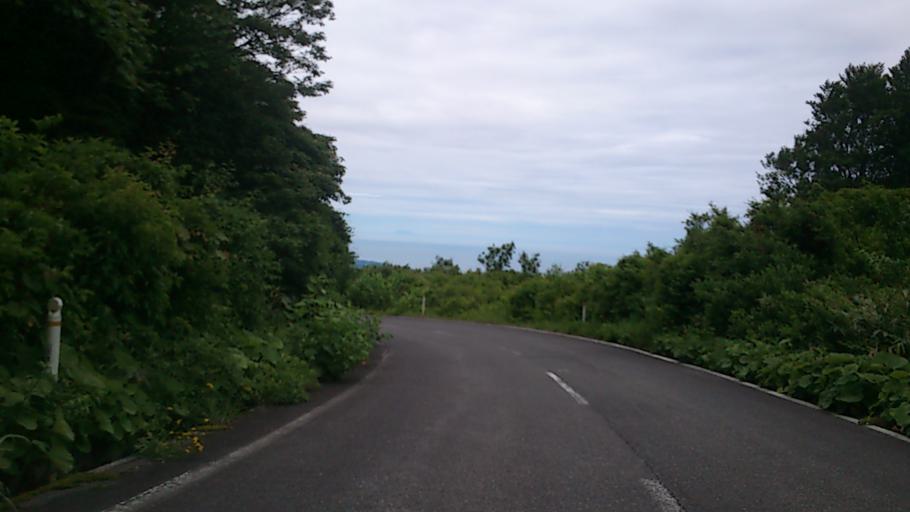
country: JP
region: Yamagata
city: Yuza
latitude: 39.1102
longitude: 139.9629
